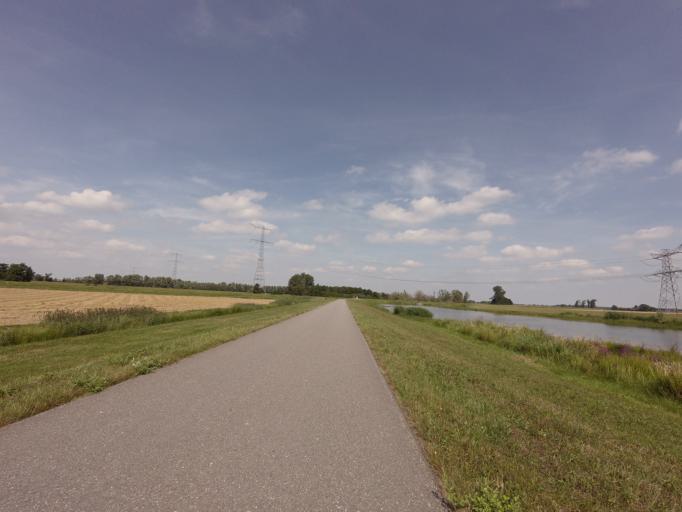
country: NL
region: South Holland
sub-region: Gemeente Sliedrecht
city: Sliedrecht
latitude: 51.7920
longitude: 4.8016
